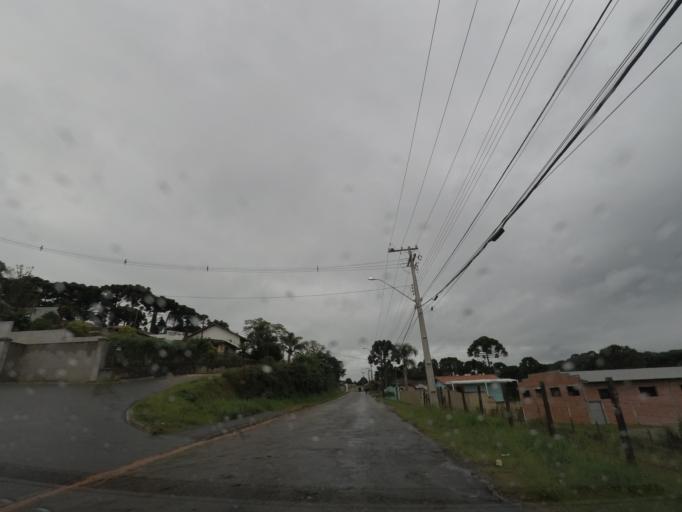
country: BR
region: Parana
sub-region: Campo Largo
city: Campo Largo
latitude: -25.4620
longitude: -49.4072
